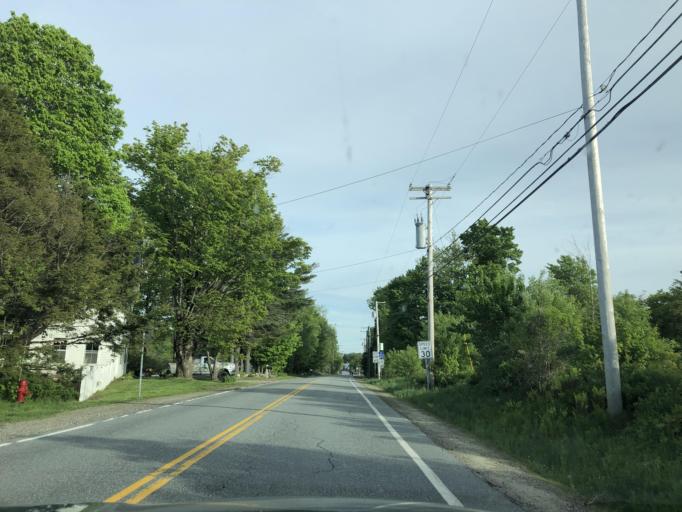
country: US
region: New Hampshire
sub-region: Merrimack County
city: New London
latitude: 43.4230
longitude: -71.9934
